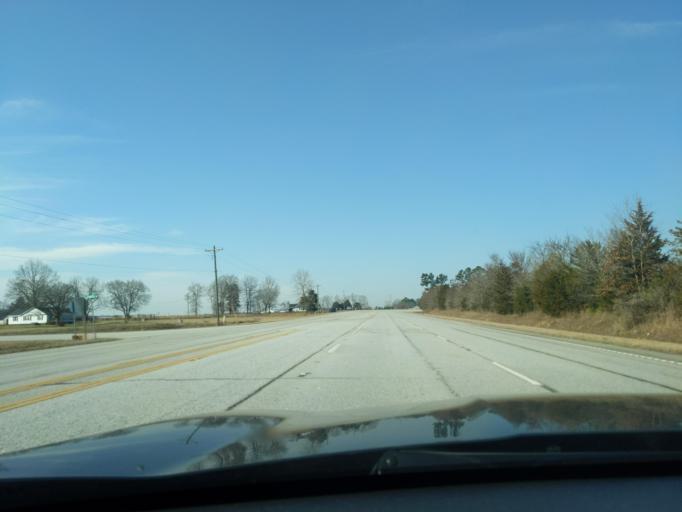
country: US
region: South Carolina
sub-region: Abbeville County
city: Calhoun Falls
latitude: 34.0956
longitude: -82.5663
